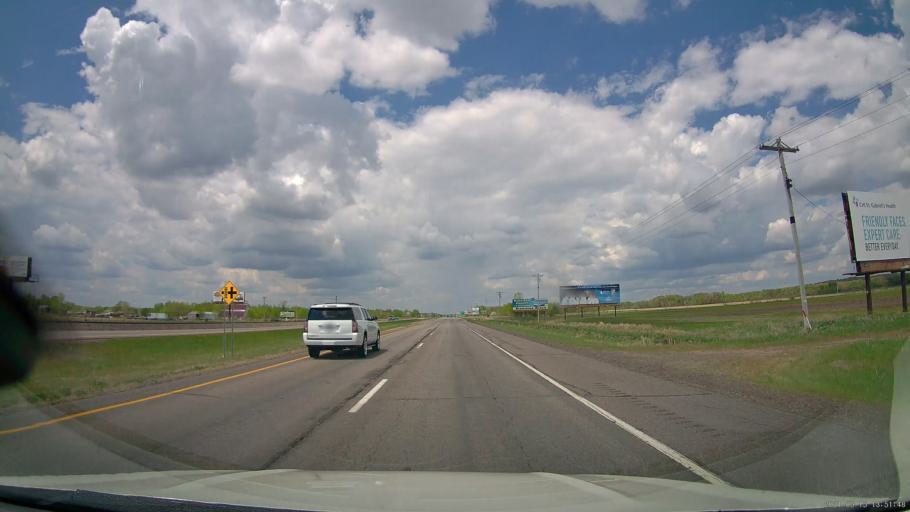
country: US
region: Minnesota
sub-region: Morrison County
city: Little Falls
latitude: 45.9095
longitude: -94.3399
